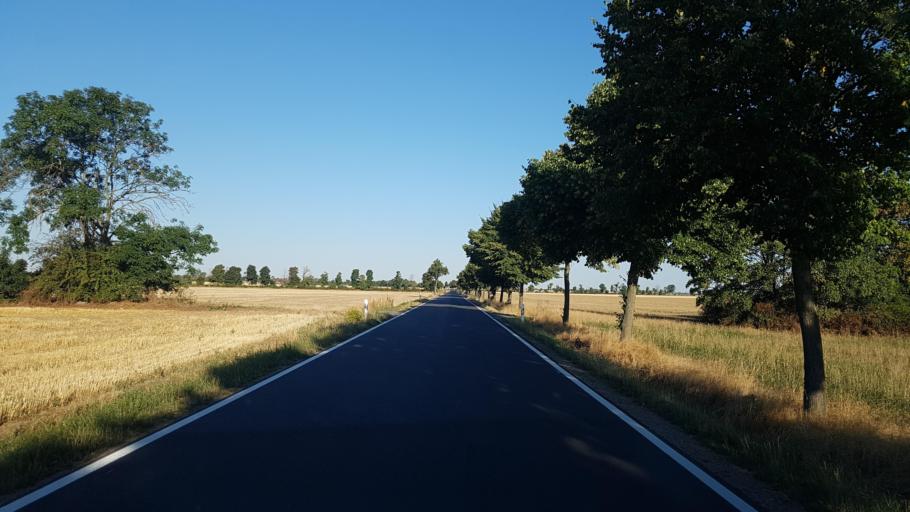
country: DE
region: Saxony
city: Dahlen
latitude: 51.3639
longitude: 12.9794
